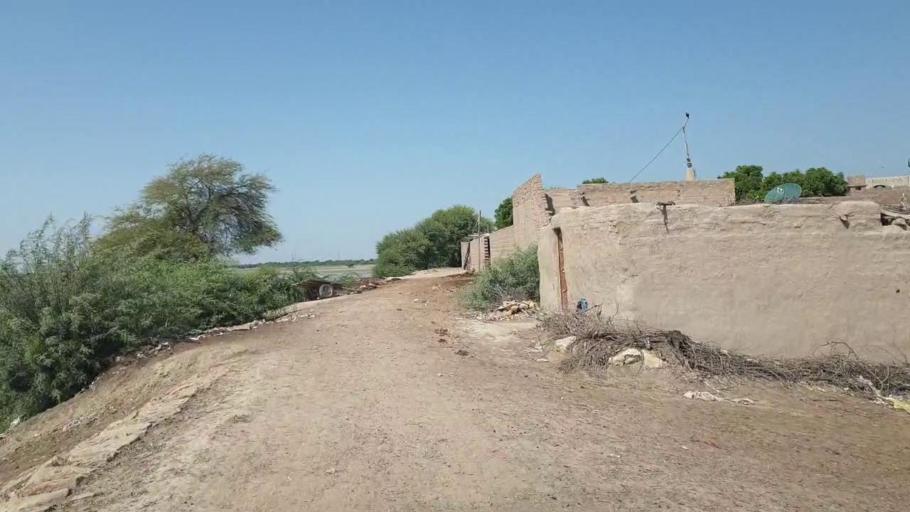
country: PK
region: Sindh
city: Matiari
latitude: 25.6478
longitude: 68.4945
